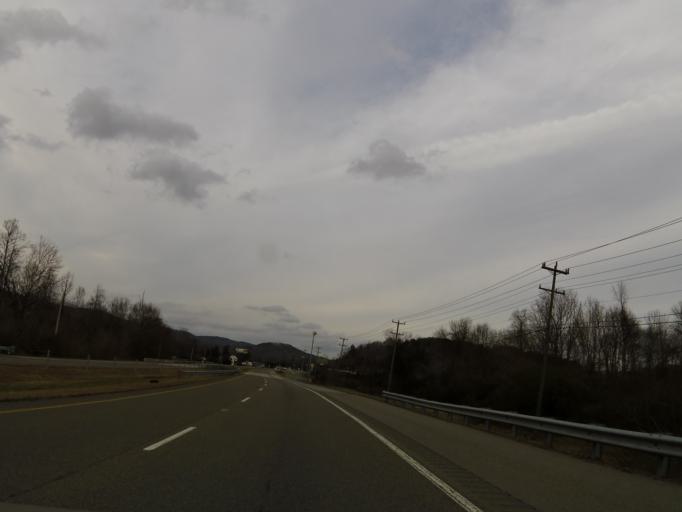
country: US
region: Tennessee
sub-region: Hamilton County
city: Sale Creek
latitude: 35.3367
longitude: -85.1295
